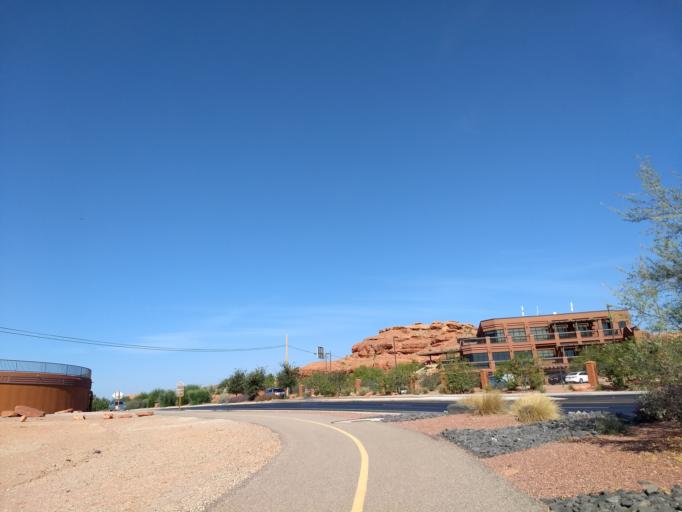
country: US
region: Utah
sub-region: Washington County
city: Saint George
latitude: 37.1127
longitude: -113.5722
